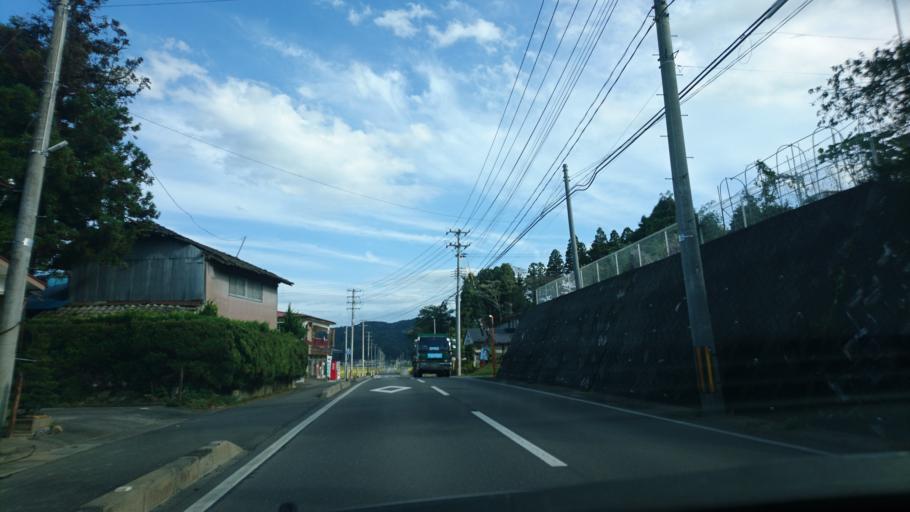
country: JP
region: Iwate
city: Ichinoseki
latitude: 38.8365
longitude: 141.2400
